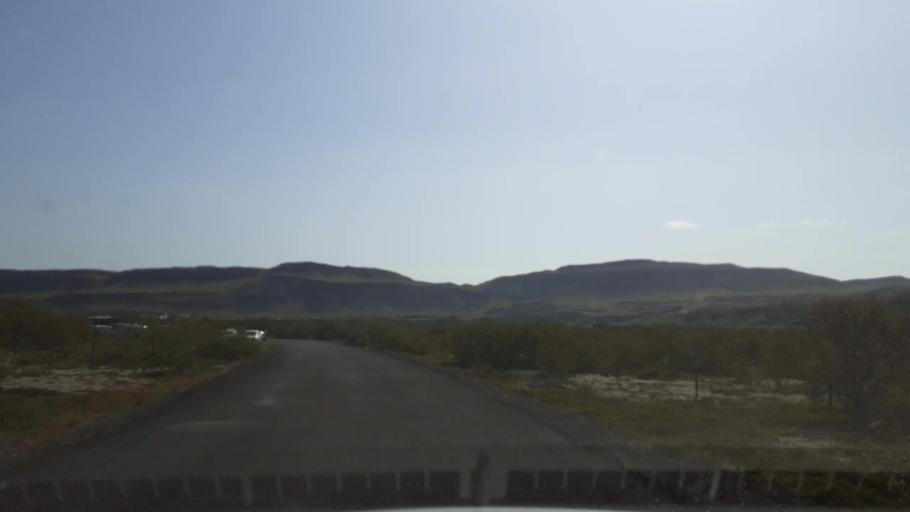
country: IS
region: West
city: Borgarnes
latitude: 64.7561
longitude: -21.5506
